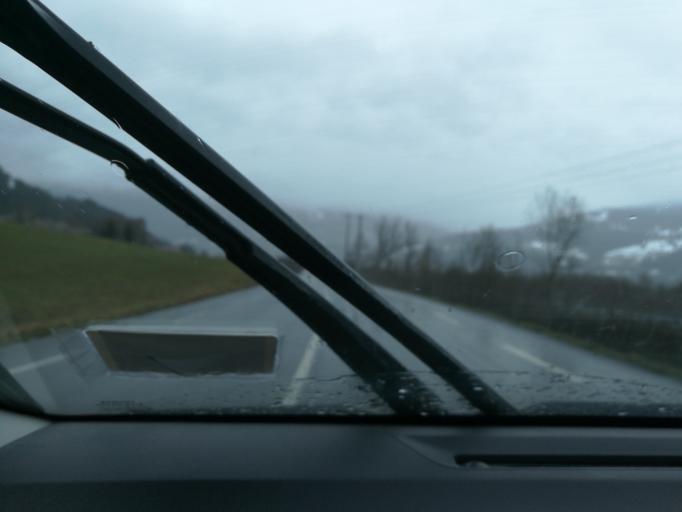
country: FR
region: Rhone-Alpes
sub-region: Departement de la Haute-Savoie
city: Domancy
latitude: 45.9244
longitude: 6.6603
